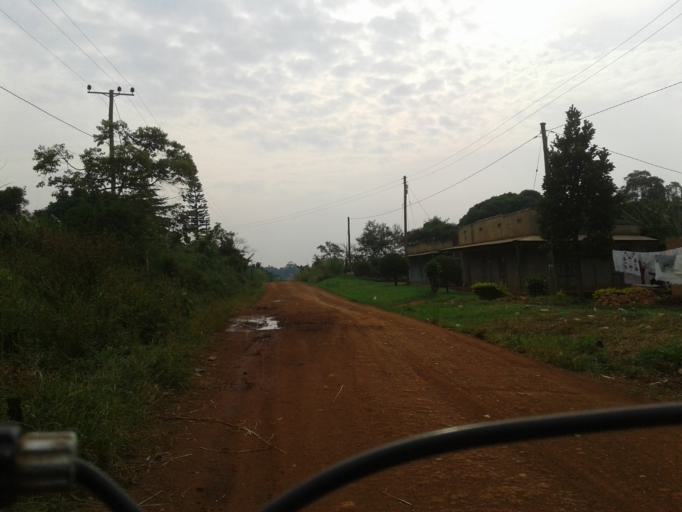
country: UG
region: Western Region
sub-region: Hoima District
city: Hoima
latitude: 1.4273
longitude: 31.3291
